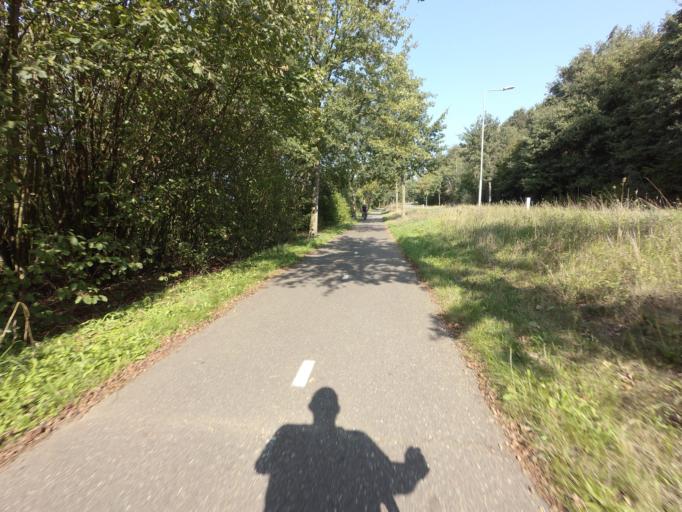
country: NL
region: Limburg
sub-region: Gemeente Maasgouw
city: Maasbracht
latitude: 51.1820
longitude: 5.8828
